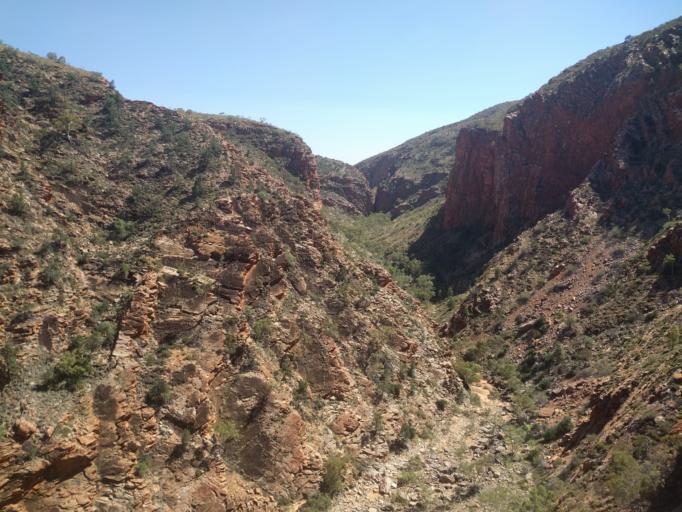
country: AU
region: Northern Territory
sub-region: Alice Springs
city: Alice Springs
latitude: -23.7502
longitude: 132.9792
